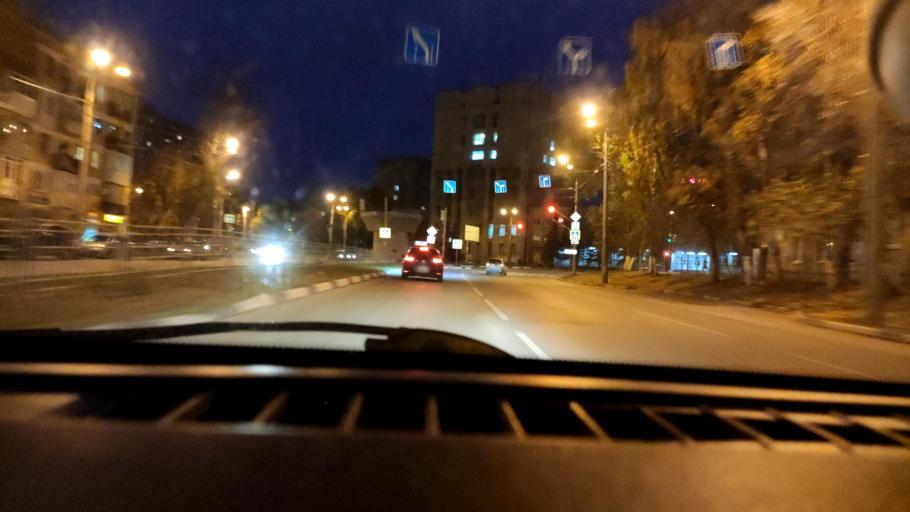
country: RU
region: Samara
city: Samara
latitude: 53.2010
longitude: 50.1628
